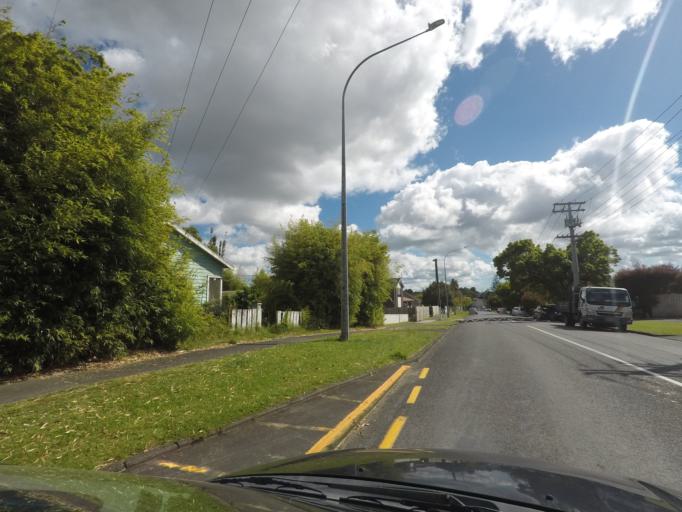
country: NZ
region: Auckland
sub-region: Auckland
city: Waitakere
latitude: -36.9147
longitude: 174.6652
